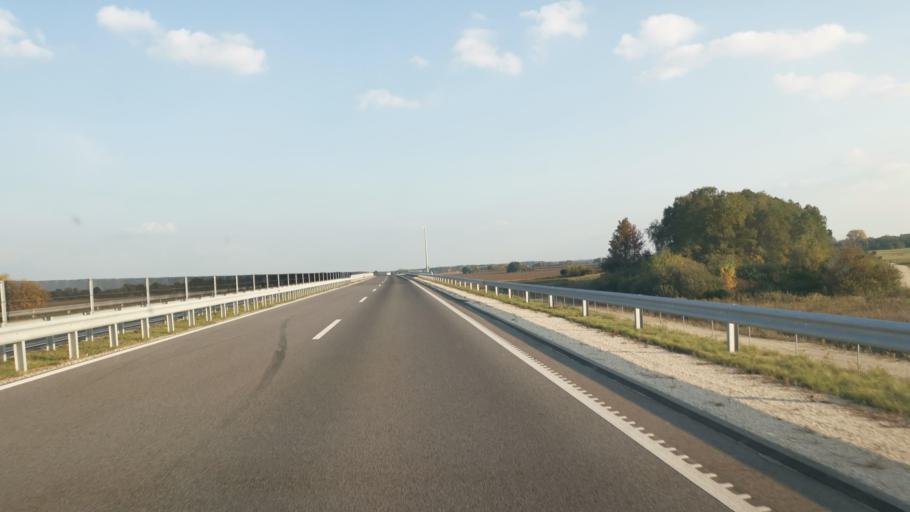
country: HU
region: Gyor-Moson-Sopron
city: Kapuvar
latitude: 47.5757
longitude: 16.9980
